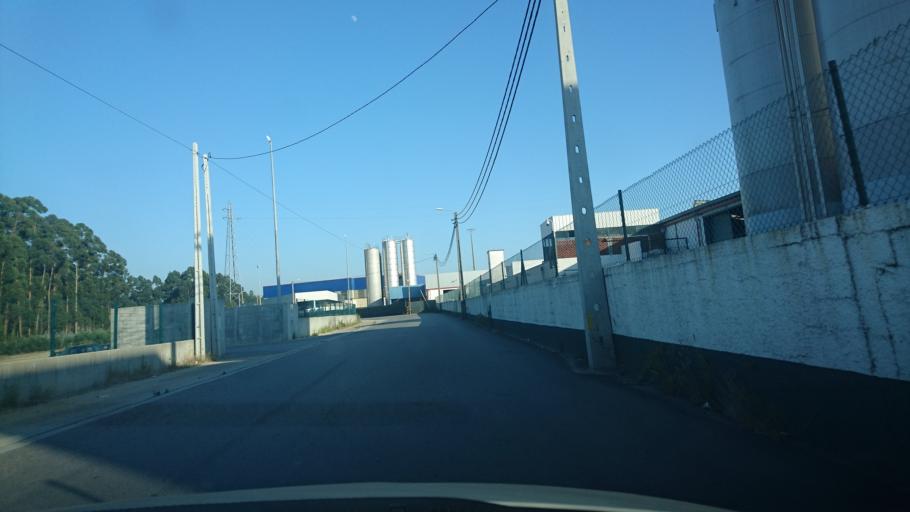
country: PT
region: Aveiro
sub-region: Ovar
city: Esmoriz
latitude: 40.9662
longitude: -8.6135
